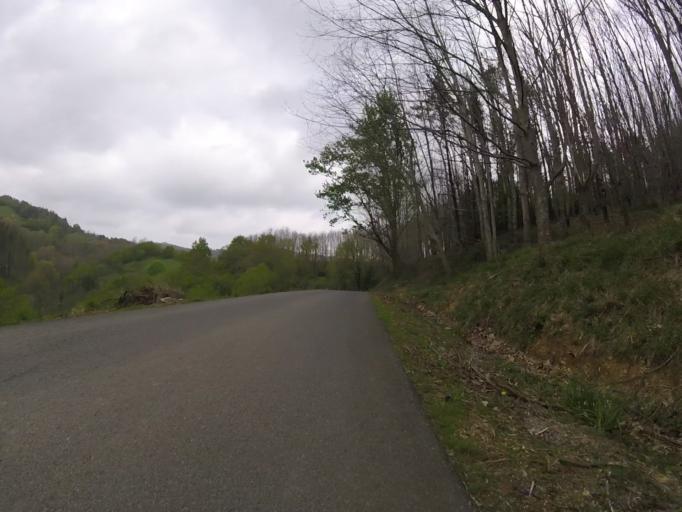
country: ES
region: Basque Country
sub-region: Provincia de Guipuzcoa
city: Zizurkil
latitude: 43.2125
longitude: -2.0849
